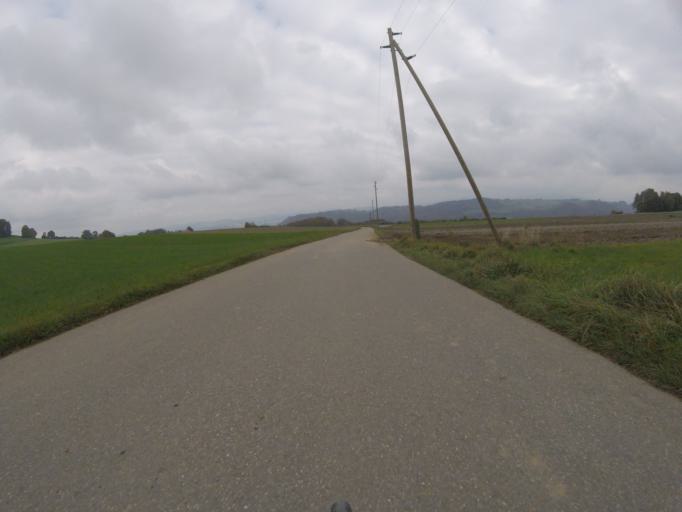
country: CH
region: Bern
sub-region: Bern-Mittelland District
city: Toffen
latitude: 46.8615
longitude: 7.4725
